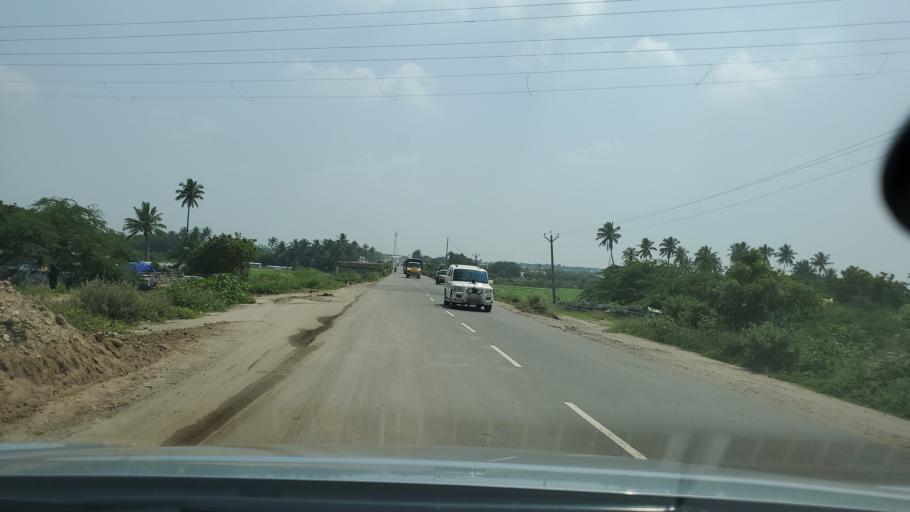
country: IN
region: Tamil Nadu
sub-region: Tiruppur
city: Dharapuram
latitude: 10.7743
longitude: 77.5085
